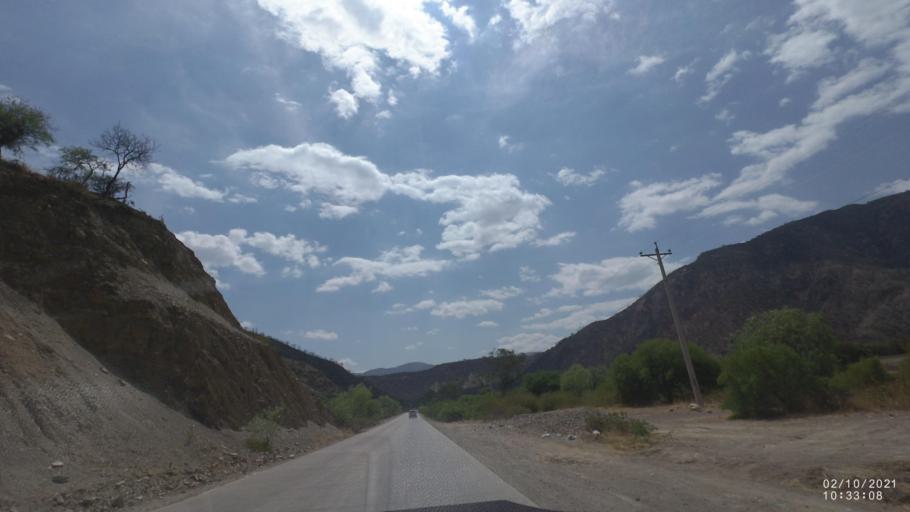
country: BO
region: Cochabamba
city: Capinota
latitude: -17.6828
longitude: -66.2572
